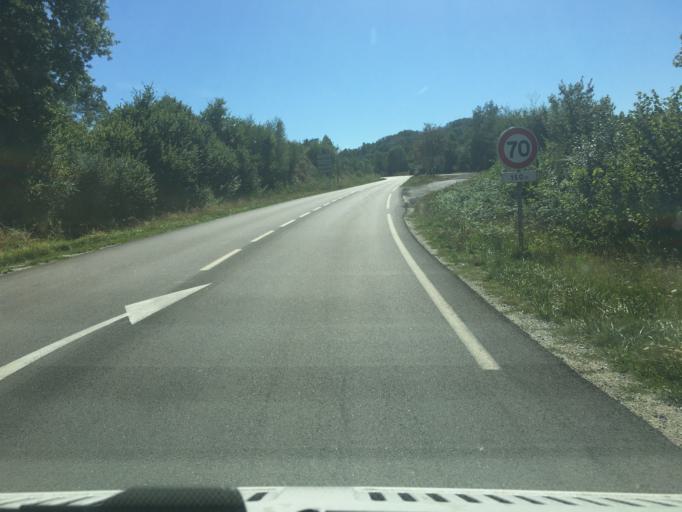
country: FR
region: Limousin
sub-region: Departement de la Correze
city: Bort-les-Orgues
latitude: 45.4232
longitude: 2.4587
